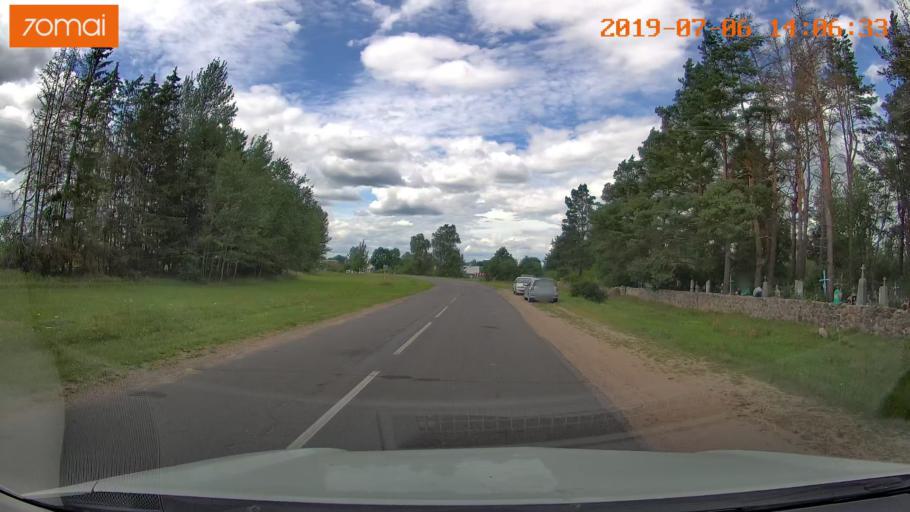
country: BY
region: Minsk
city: Ivyanyets
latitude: 53.8630
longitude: 26.7814
